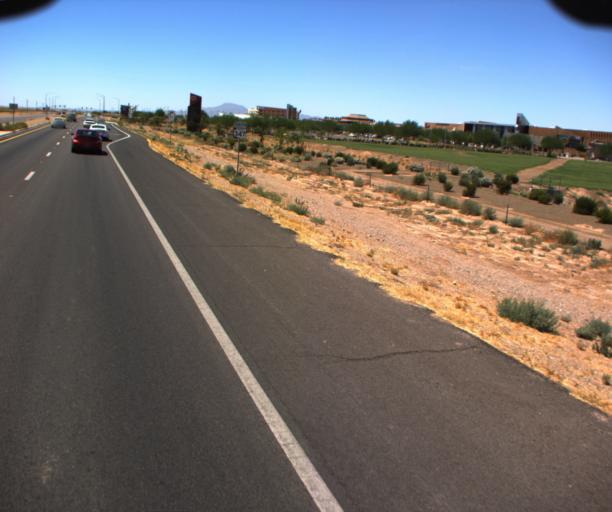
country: US
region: Arizona
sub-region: Pinal County
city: Maricopa
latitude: 33.0288
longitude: -112.0479
